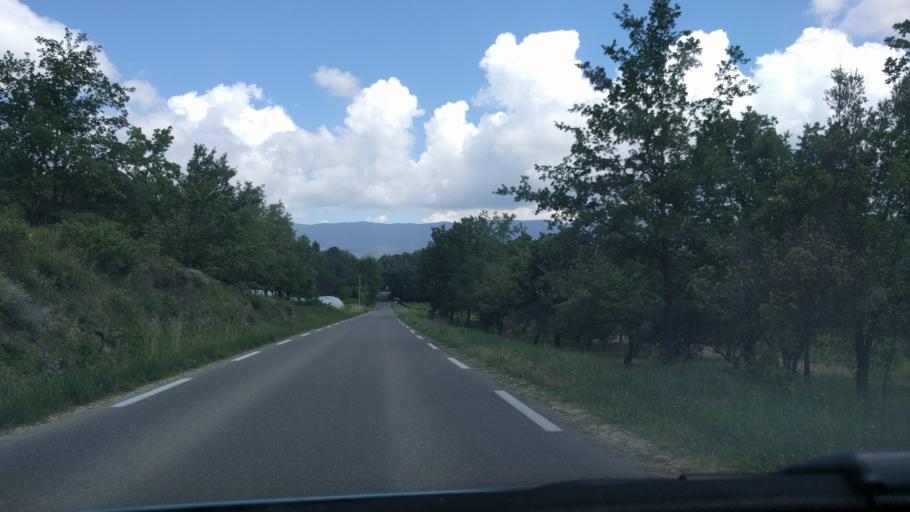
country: FR
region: Provence-Alpes-Cote d'Azur
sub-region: Departement du Vaucluse
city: Pertuis
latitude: 43.7429
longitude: 5.5264
